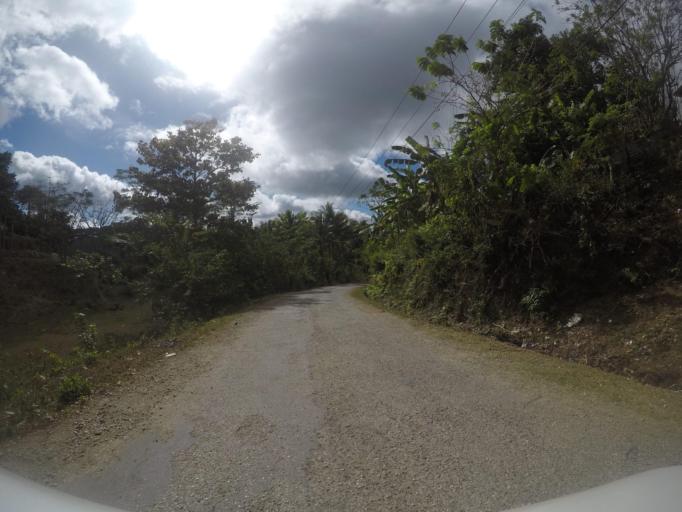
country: TL
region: Lautem
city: Lospalos
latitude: -8.5342
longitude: 126.9349
